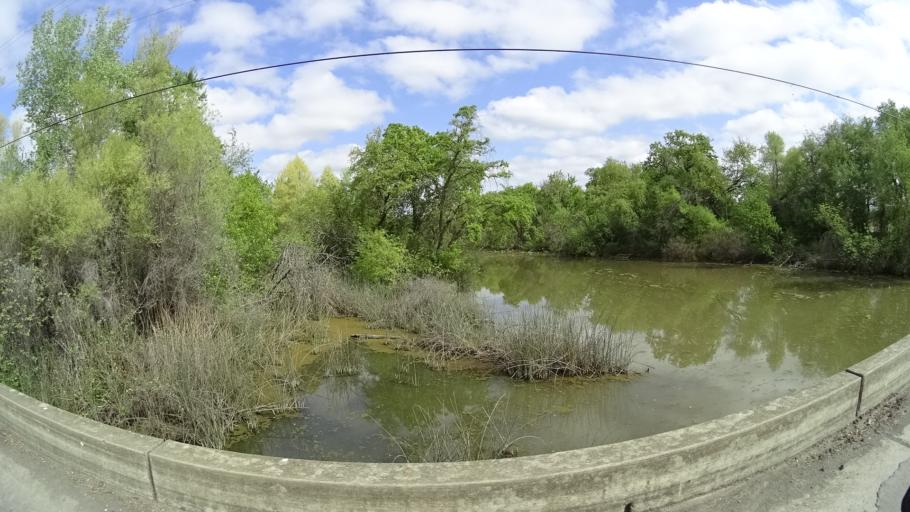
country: US
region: California
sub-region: Butte County
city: Biggs
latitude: 39.4199
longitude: -121.8930
